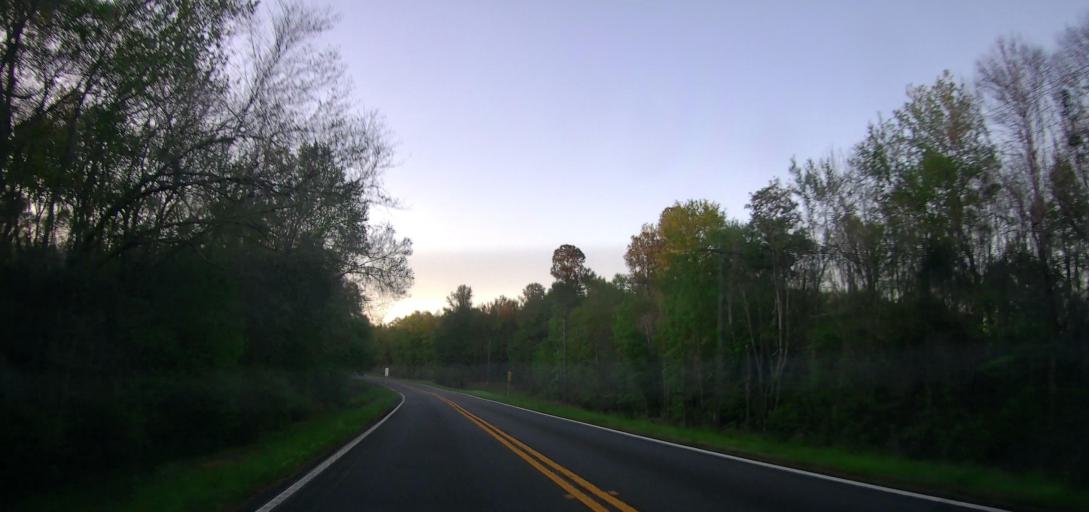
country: US
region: Georgia
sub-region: Marion County
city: Buena Vista
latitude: 32.4219
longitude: -84.5889
